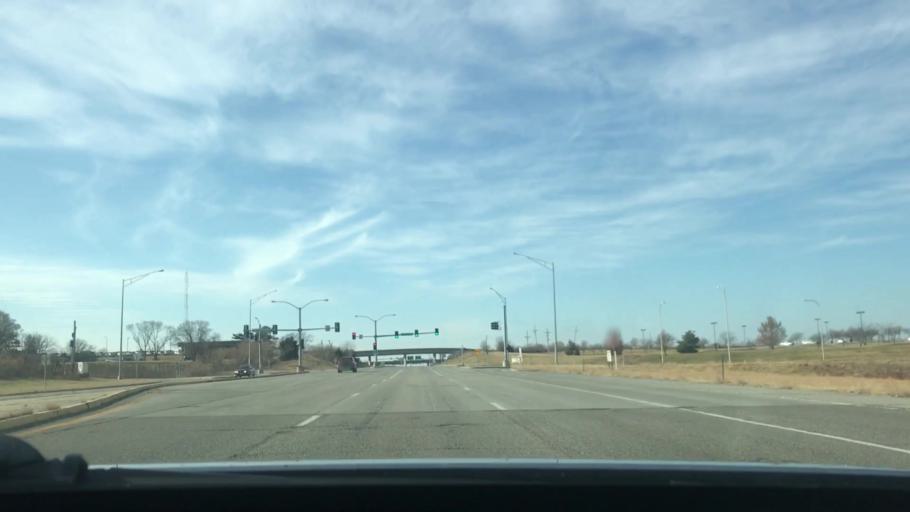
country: US
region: Missouri
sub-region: Platte County
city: Weatherby Lake
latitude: 39.3112
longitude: -94.6806
